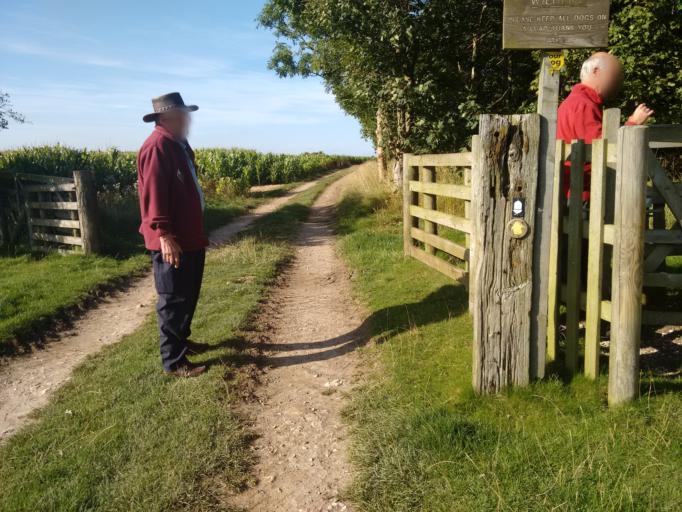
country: GB
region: England
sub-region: North Yorkshire
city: Thixendale
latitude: 54.0432
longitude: -0.7225
